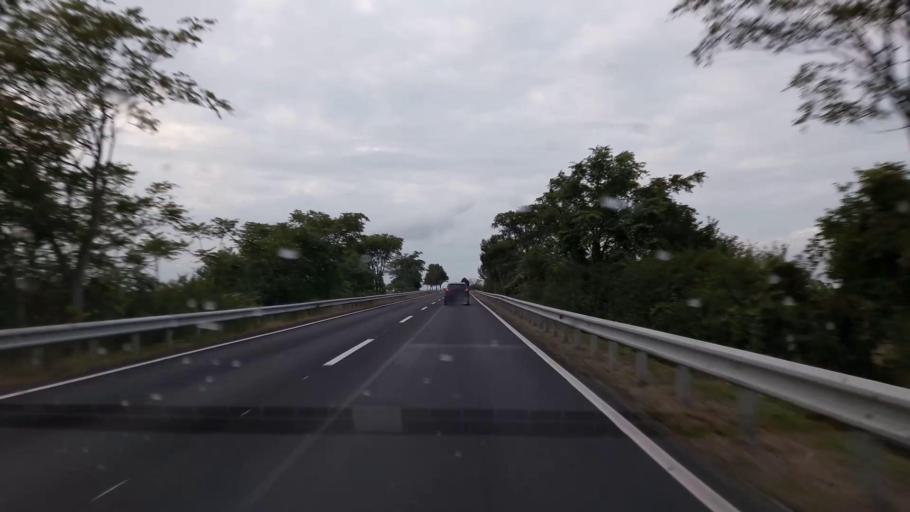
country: AT
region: Lower Austria
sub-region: Politischer Bezirk Wien-Umgebung
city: Schwadorf
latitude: 48.0825
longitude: 16.5662
